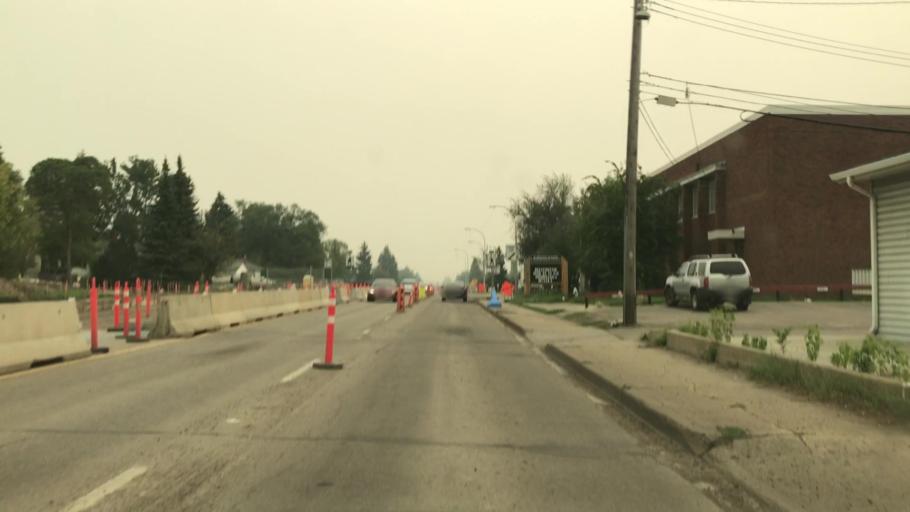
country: CA
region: Alberta
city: Edmonton
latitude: 53.5148
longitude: -113.4552
